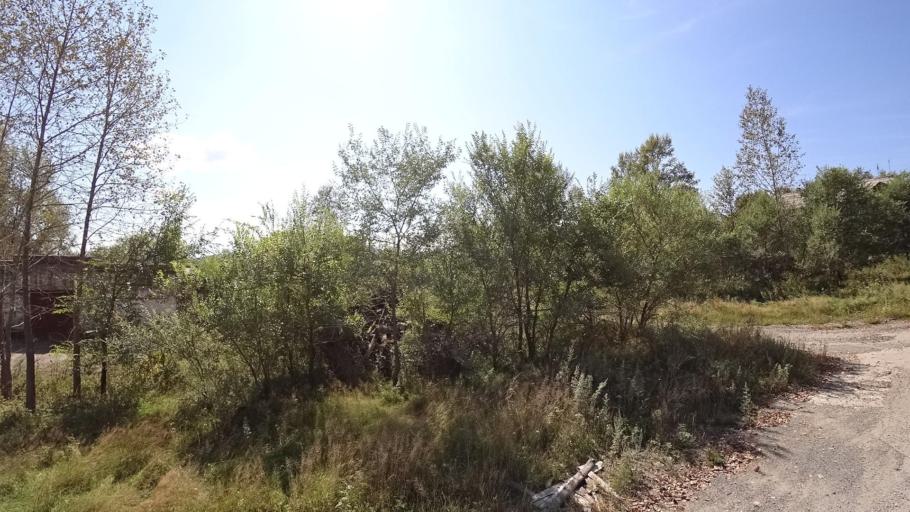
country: RU
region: Jewish Autonomous Oblast
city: Londoko
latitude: 49.0058
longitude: 131.8860
